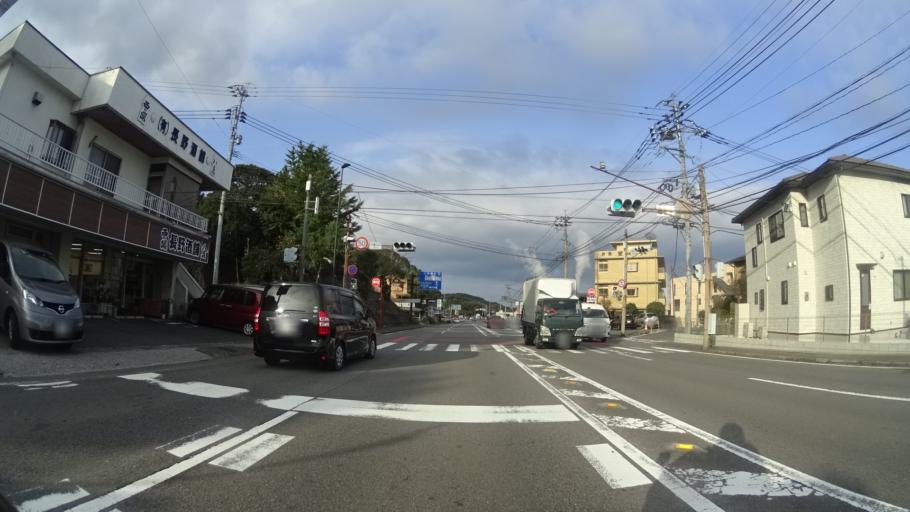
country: JP
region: Oita
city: Beppu
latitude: 33.3082
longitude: 131.4628
